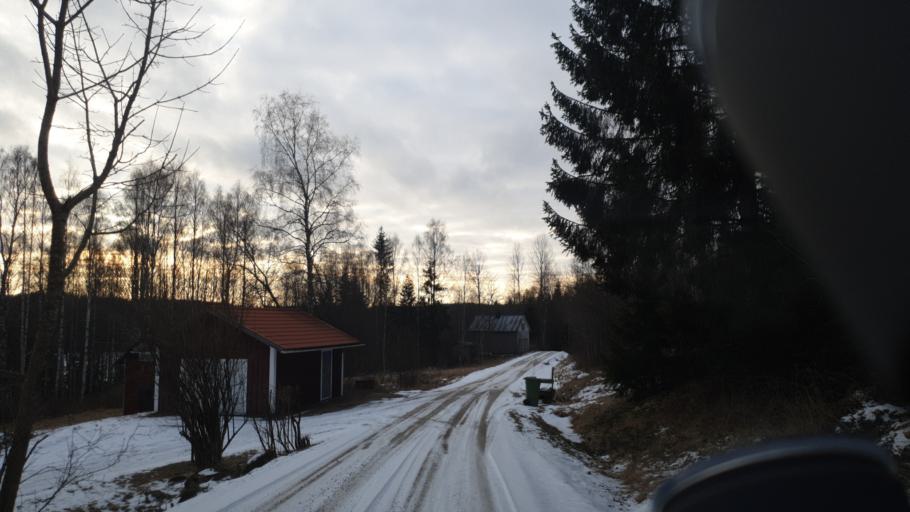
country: SE
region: Vaermland
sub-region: Eda Kommun
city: Amotfors
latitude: 59.7996
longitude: 12.4236
